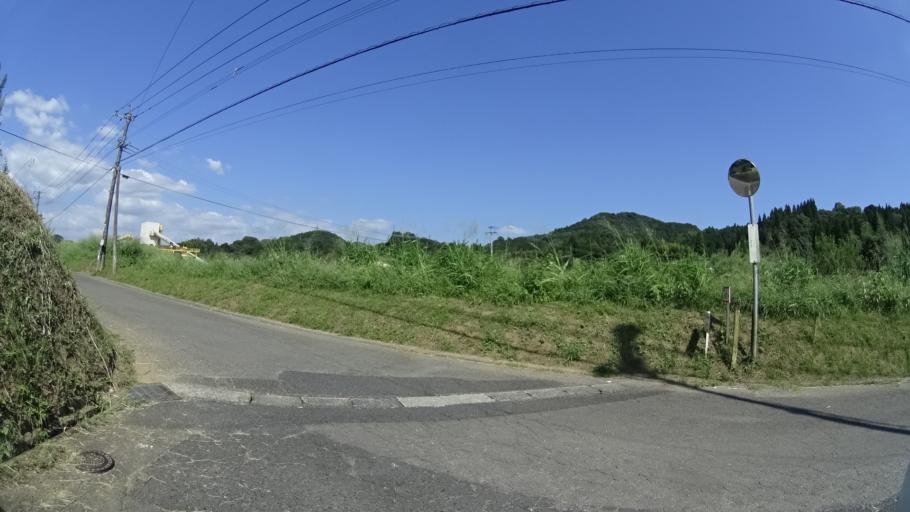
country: JP
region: Kagoshima
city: Kajiki
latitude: 31.7556
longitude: 130.6747
